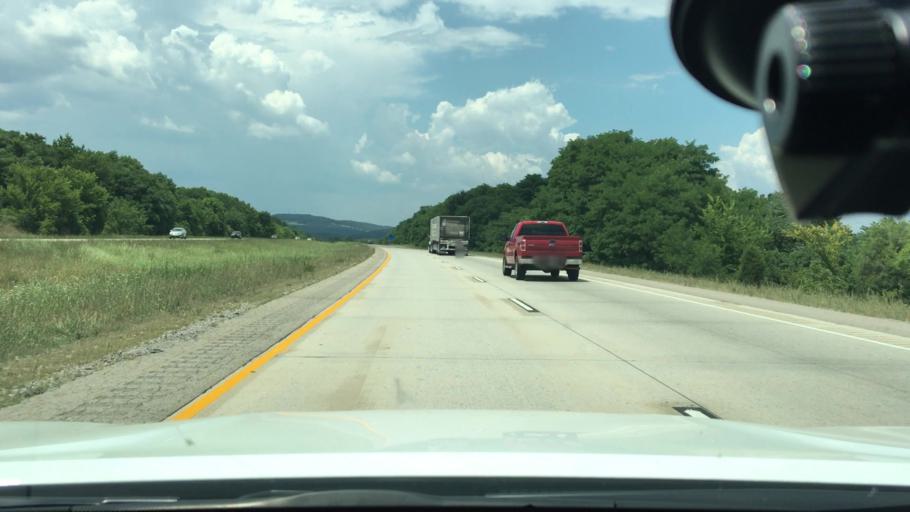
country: US
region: Arkansas
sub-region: Washington County
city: Greenland
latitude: 35.9686
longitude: -94.1964
